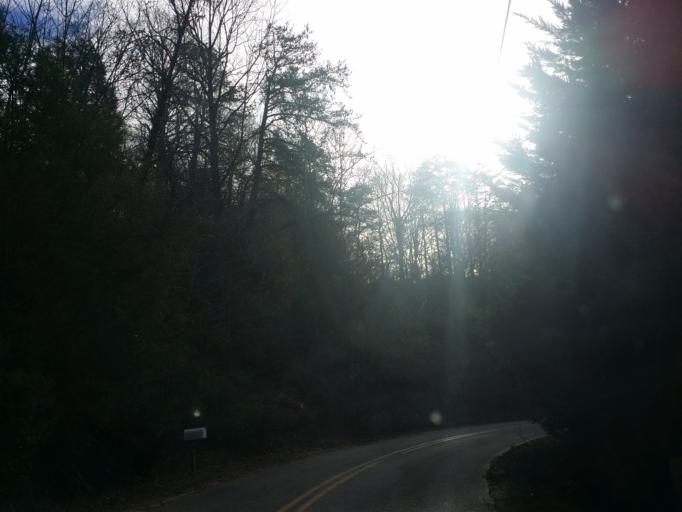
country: US
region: North Carolina
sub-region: Buncombe County
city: Swannanoa
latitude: 35.6342
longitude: -82.4173
